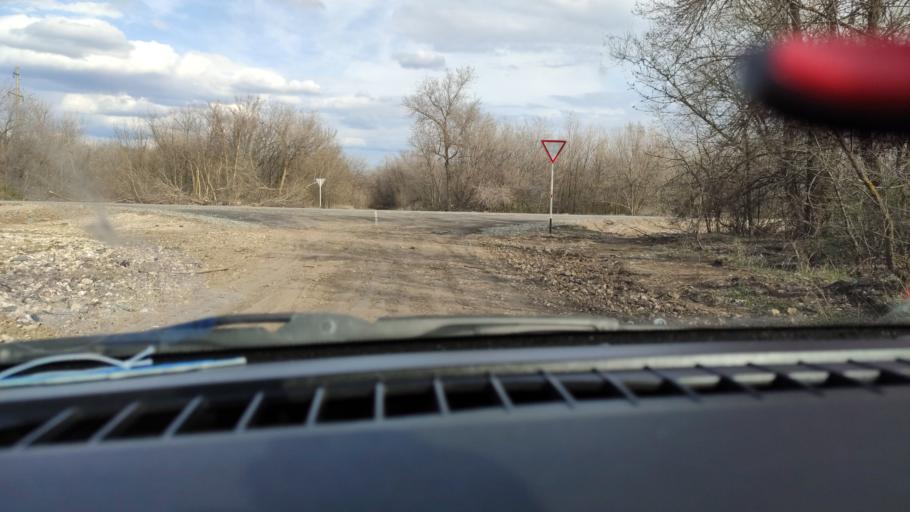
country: RU
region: Saratov
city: Privolzhskiy
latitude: 51.1403
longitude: 45.9605
